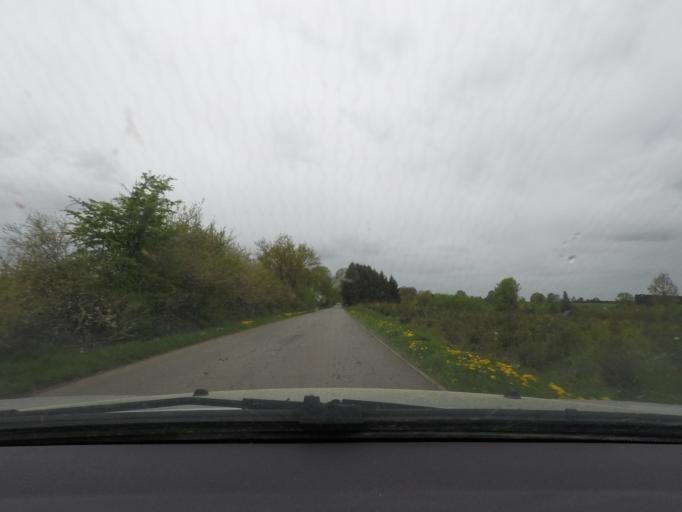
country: BE
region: Wallonia
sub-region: Province du Luxembourg
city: Etalle
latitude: 49.7135
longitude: 5.5662
